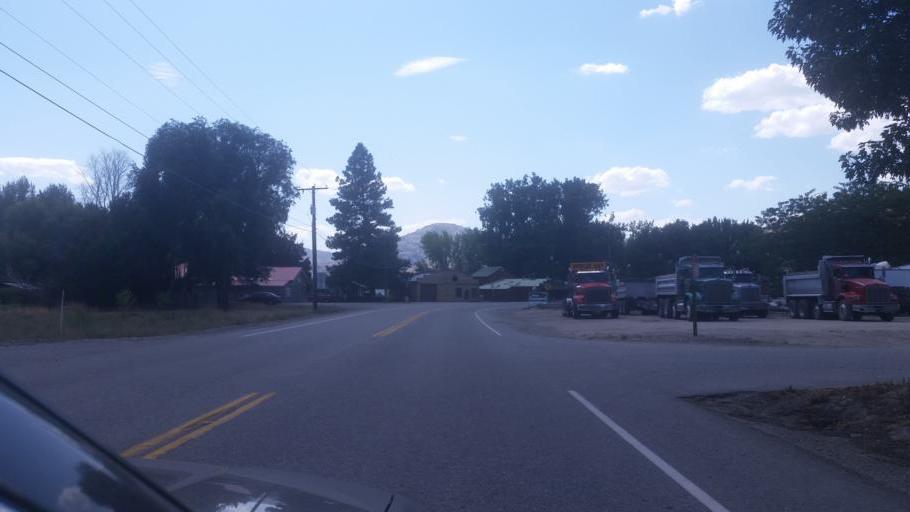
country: US
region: Washington
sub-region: Okanogan County
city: Okanogan
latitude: 48.2837
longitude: -119.7051
